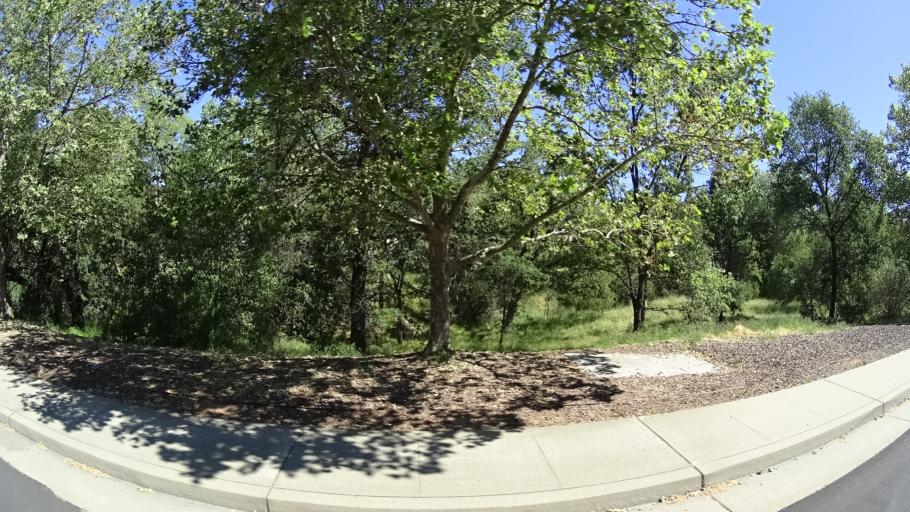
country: US
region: California
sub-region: Placer County
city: Rocklin
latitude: 38.7720
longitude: -121.2226
